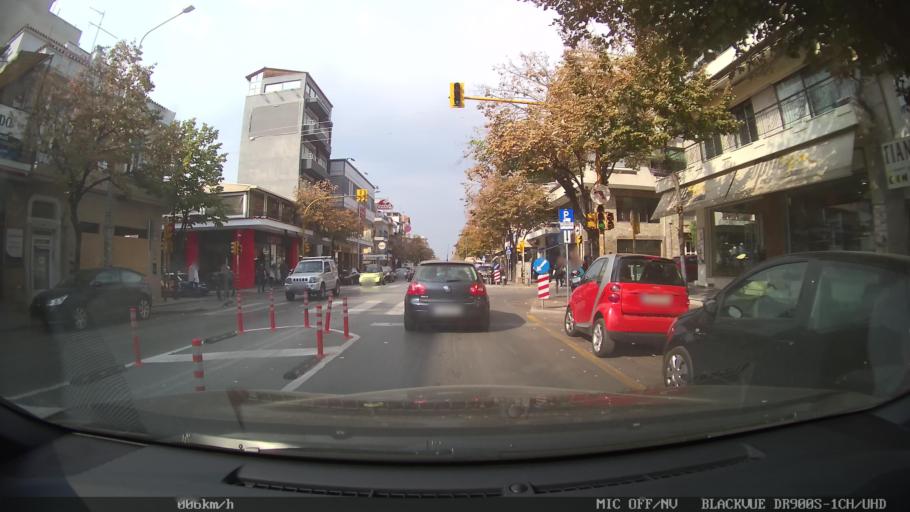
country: GR
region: Central Macedonia
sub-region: Nomos Thessalonikis
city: Triandria
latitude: 40.6147
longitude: 22.9778
